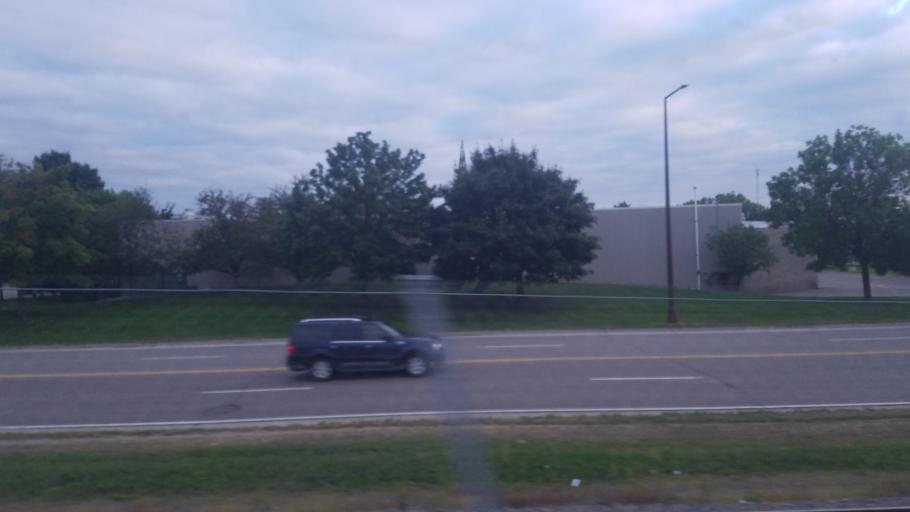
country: US
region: Minnesota
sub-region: Ramsey County
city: Falcon Heights
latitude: 44.9740
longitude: -93.1849
